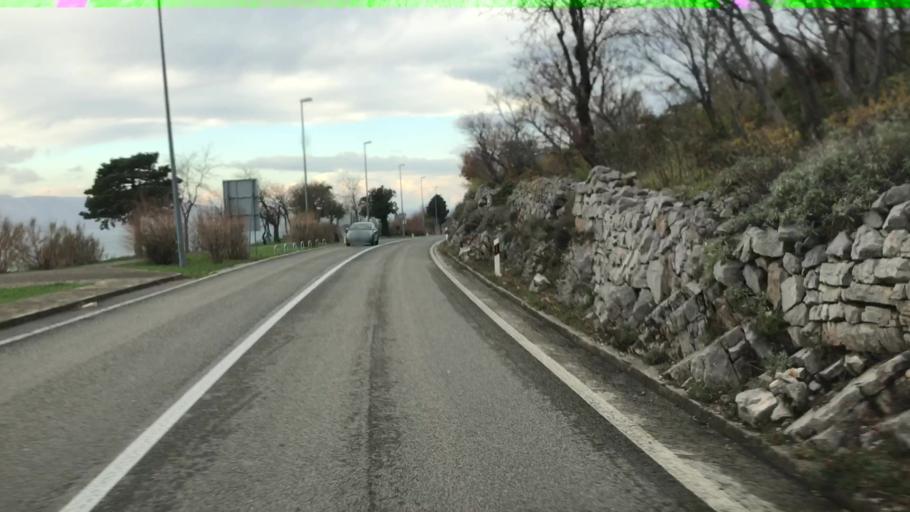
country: HR
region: Licko-Senjska
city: Senj
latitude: 44.9852
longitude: 14.9031
